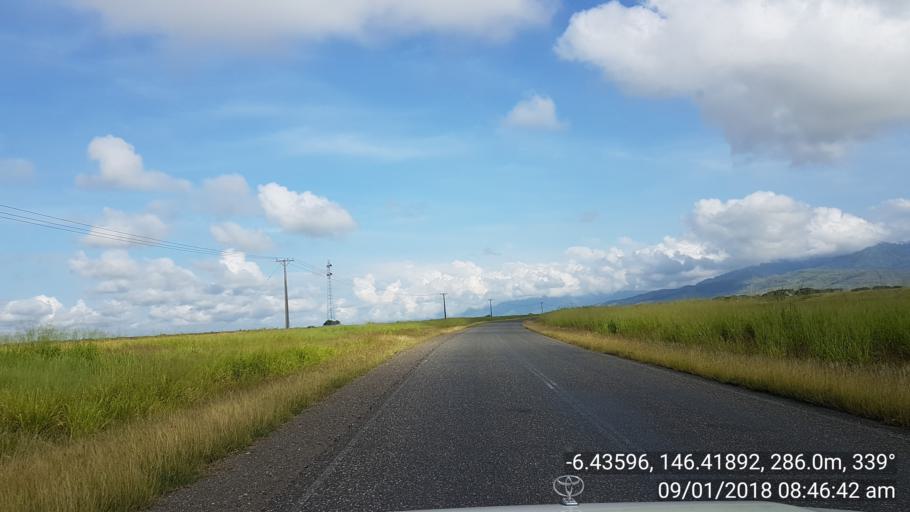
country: PG
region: Eastern Highlands
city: Kainantu
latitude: -6.4367
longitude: 146.4193
